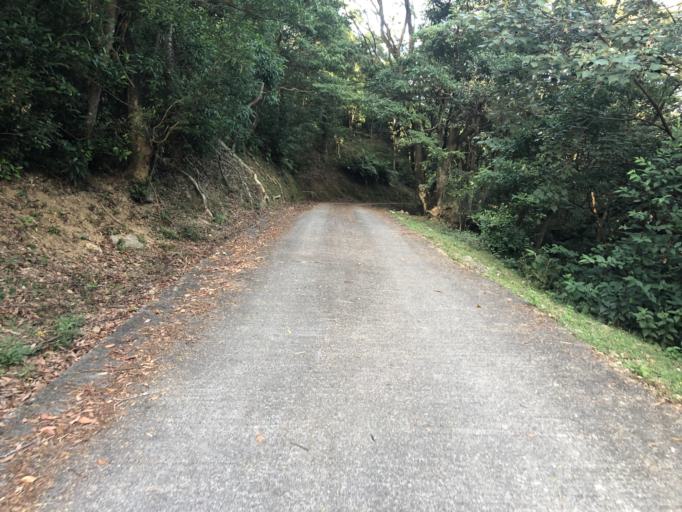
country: HK
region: Tsuen Wan
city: Tsuen Wan
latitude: 22.3919
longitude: 114.0856
